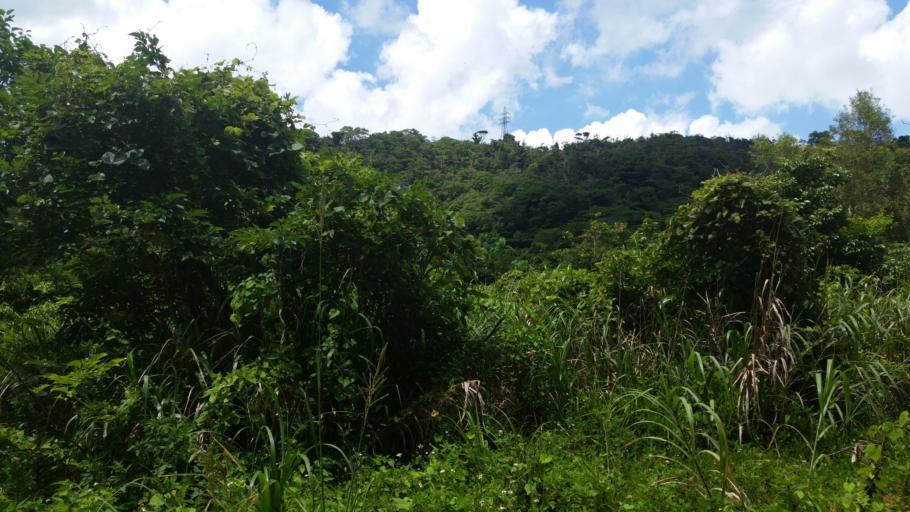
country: JP
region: Okinawa
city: Nago
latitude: 26.6356
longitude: 128.0940
